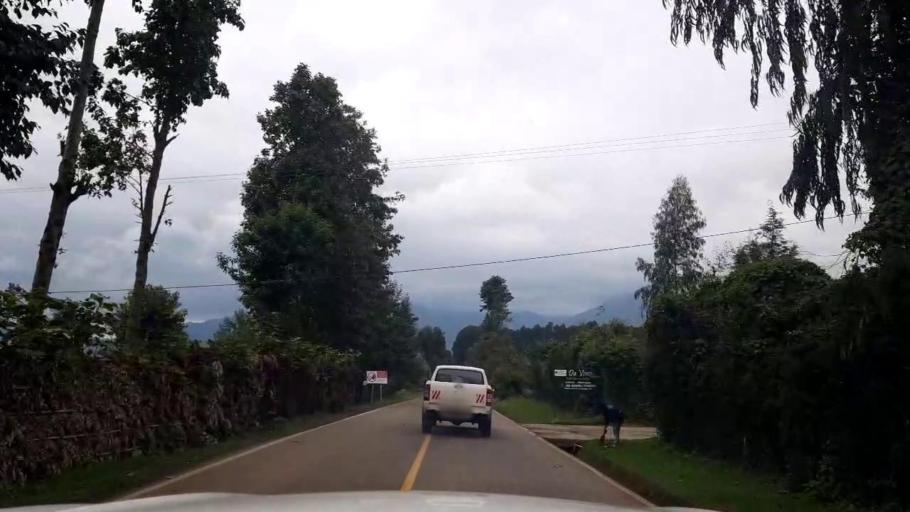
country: RW
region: Northern Province
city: Musanze
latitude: -1.4302
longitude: 29.5615
